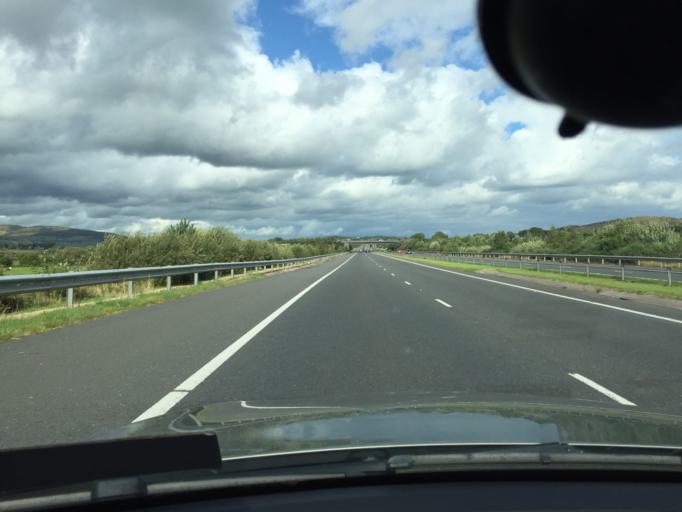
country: GB
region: Northern Ireland
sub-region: Newry and Mourne District
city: Newry
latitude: 54.1156
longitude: -6.3644
